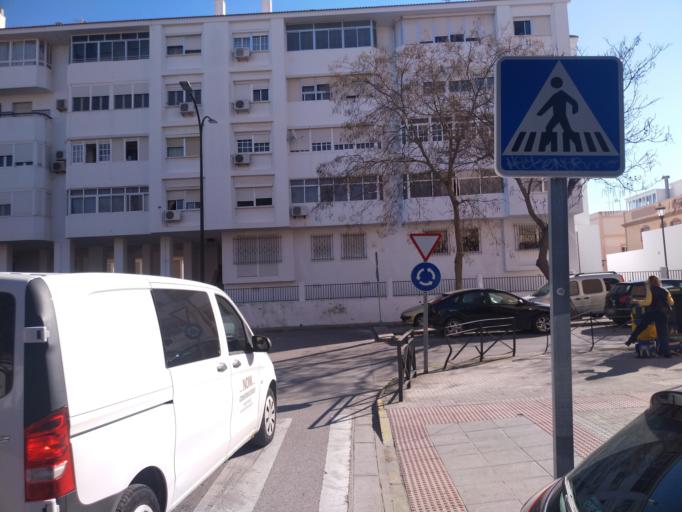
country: ES
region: Andalusia
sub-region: Provincia de Cadiz
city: San Fernando
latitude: 36.4722
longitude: -6.1926
